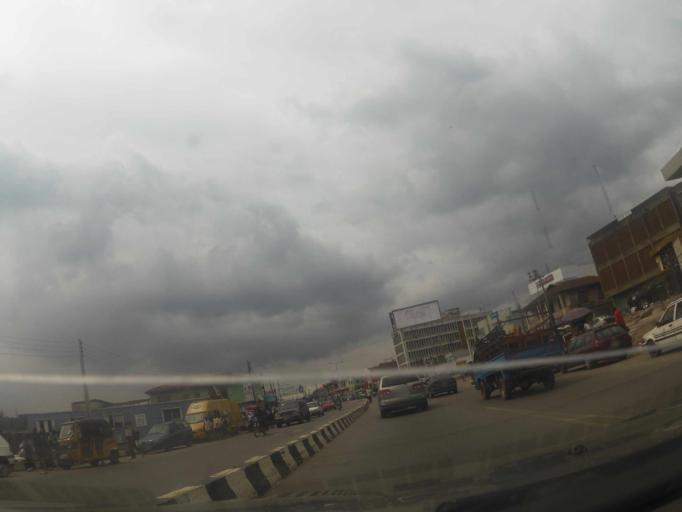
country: NG
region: Oyo
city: Ibadan
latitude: 7.4028
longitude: 3.8902
